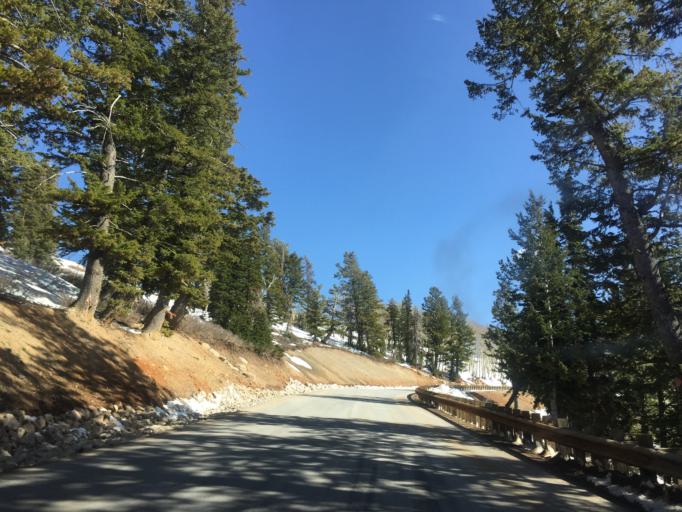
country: US
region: Utah
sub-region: Weber County
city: Wolf Creek
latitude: 41.3724
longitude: -111.7702
